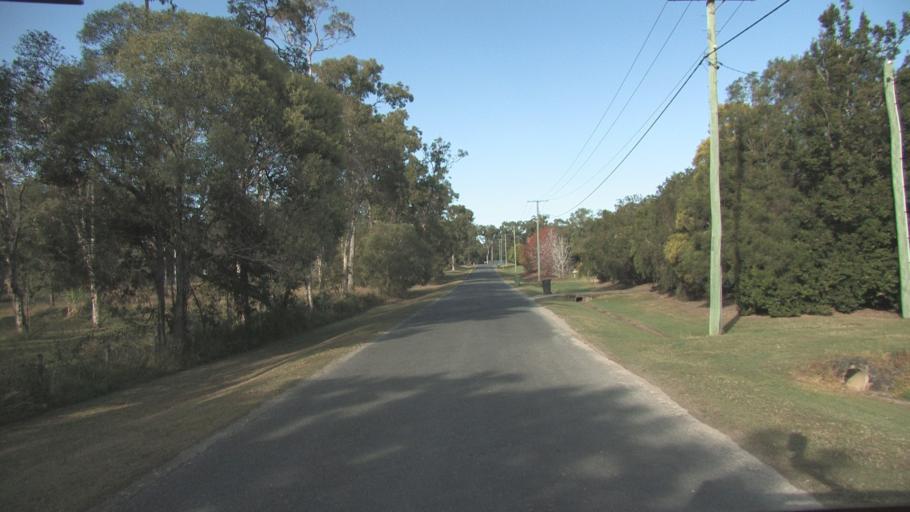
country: AU
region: Queensland
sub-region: Logan
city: Park Ridge South
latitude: -27.7440
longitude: 153.0294
